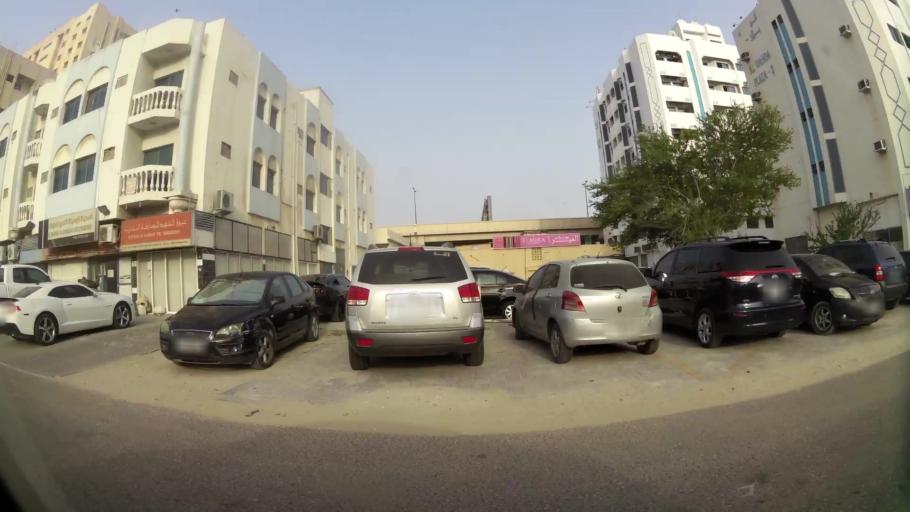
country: AE
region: Ash Shariqah
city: Sharjah
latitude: 25.3414
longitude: 55.4028
